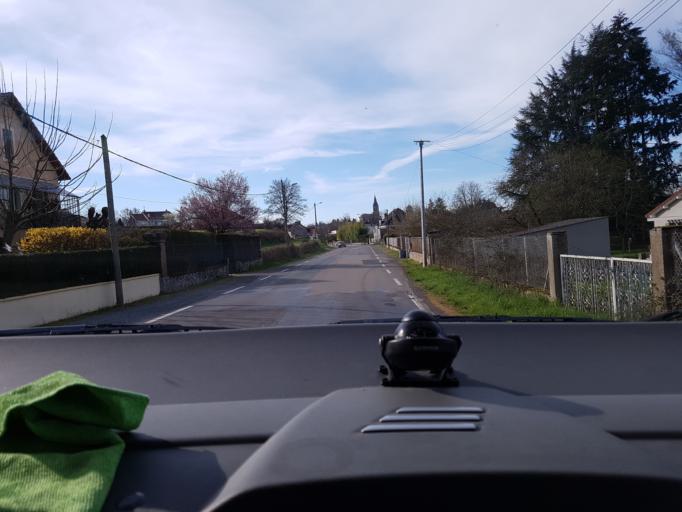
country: FR
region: Bourgogne
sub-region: Departement de Saone-et-Loire
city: Toulon-sur-Arroux
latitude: 46.6986
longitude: 4.1390
